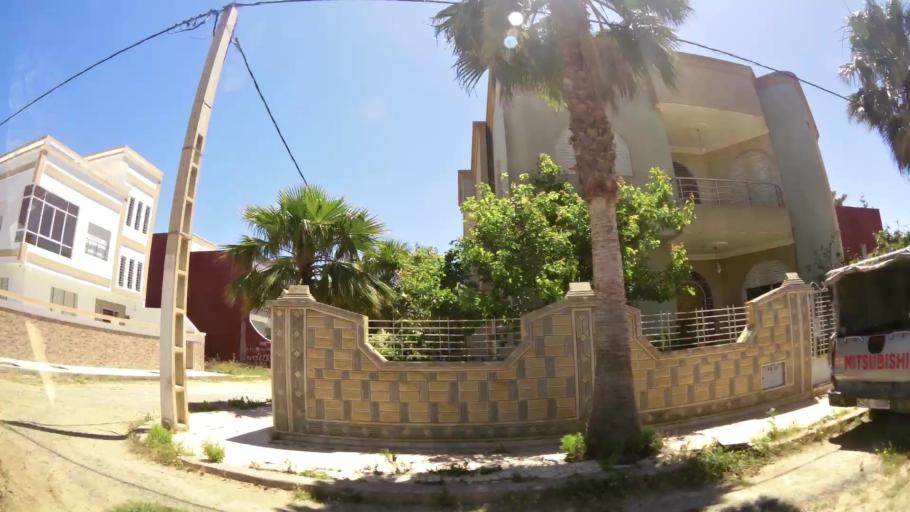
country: MA
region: Oriental
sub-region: Berkane-Taourirt
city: Madagh
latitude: 35.0867
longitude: -2.2446
